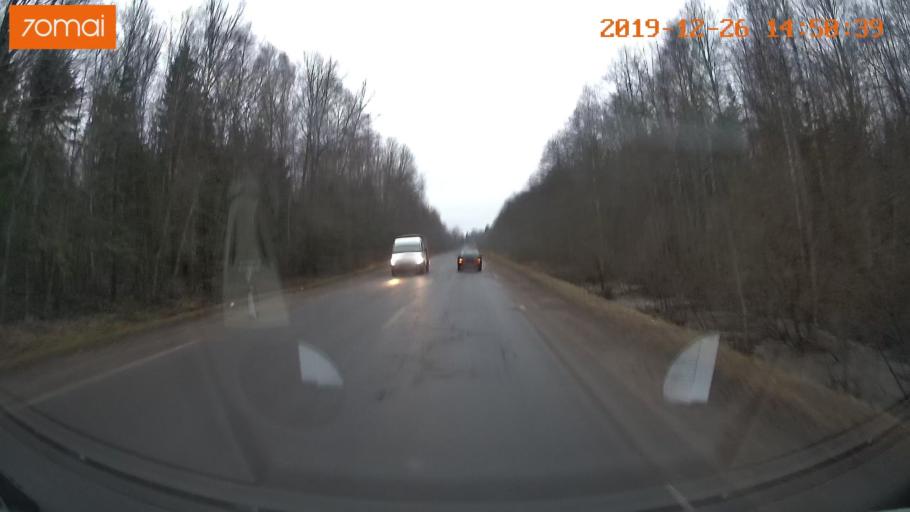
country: RU
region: Jaroslavl
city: Poshekhon'ye
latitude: 58.3303
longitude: 38.9220
